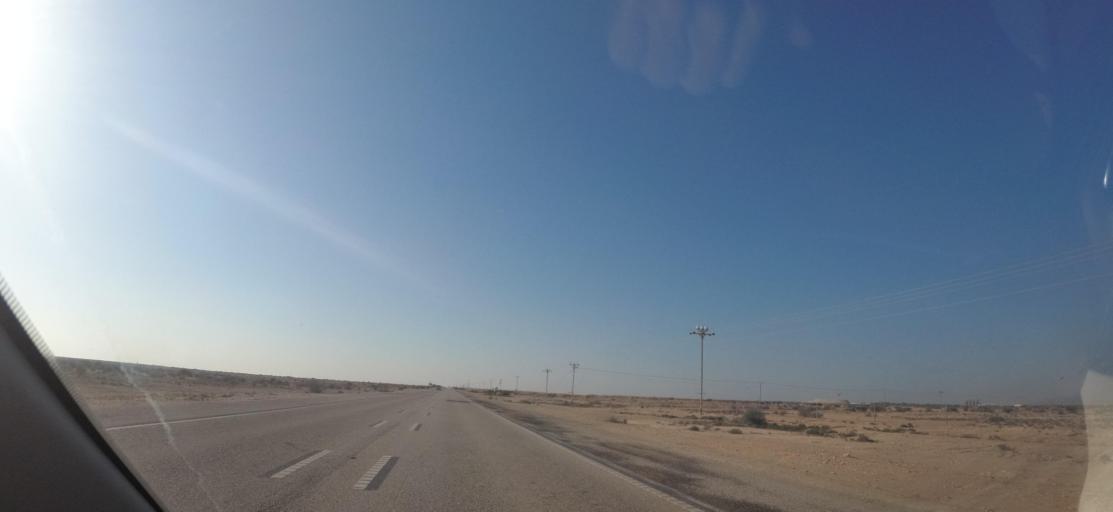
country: QA
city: Al Ghuwayriyah
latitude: 25.8573
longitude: 51.2514
